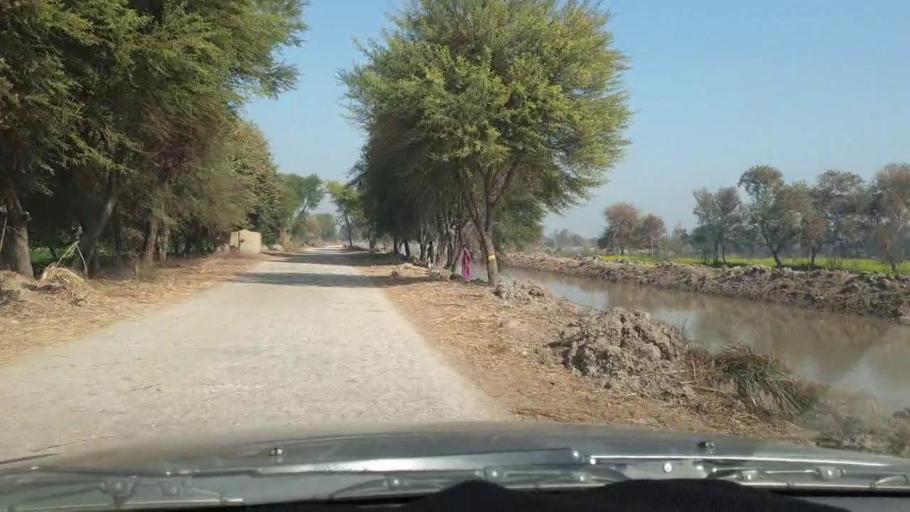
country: PK
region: Sindh
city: Khanpur
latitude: 27.7733
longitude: 69.5357
